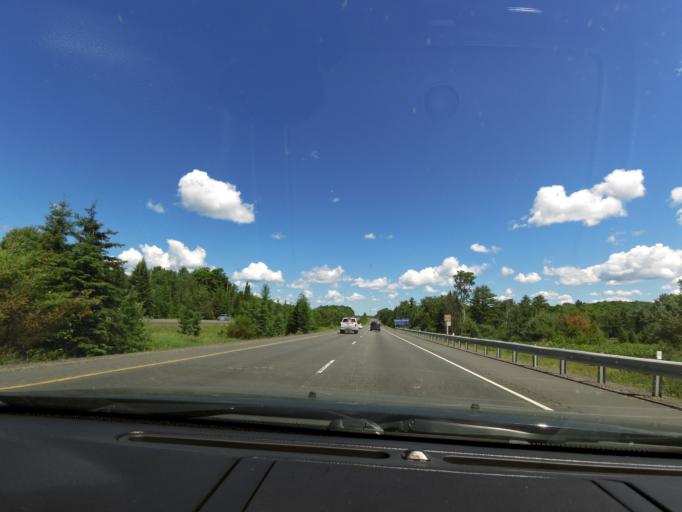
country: CA
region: Ontario
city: Bracebridge
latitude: 45.1792
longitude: -79.3120
